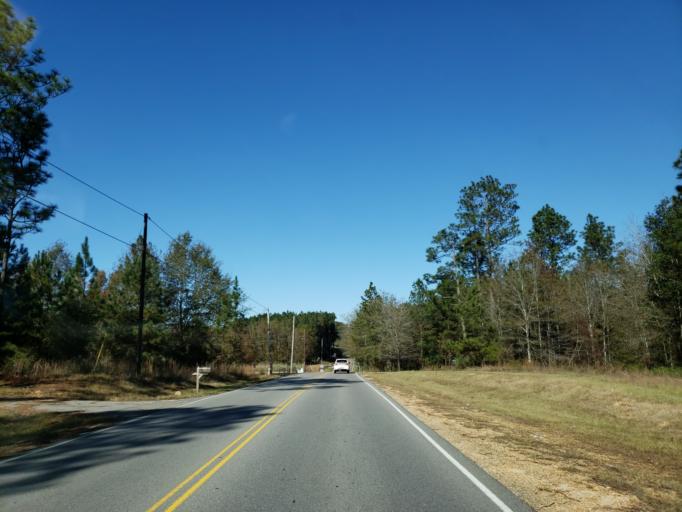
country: US
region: Mississippi
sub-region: Lamar County
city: Arnold Line
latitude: 31.3431
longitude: -89.3990
